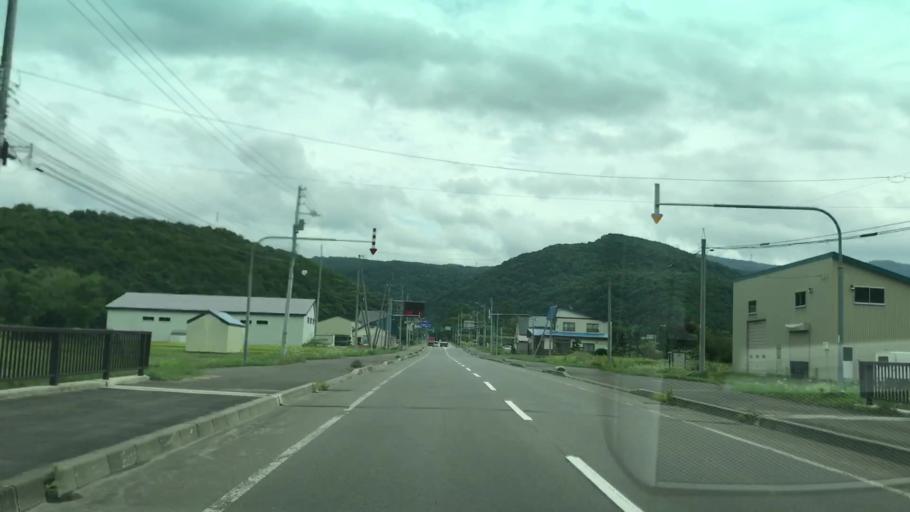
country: JP
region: Hokkaido
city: Yoichi
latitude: 43.0506
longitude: 140.8404
